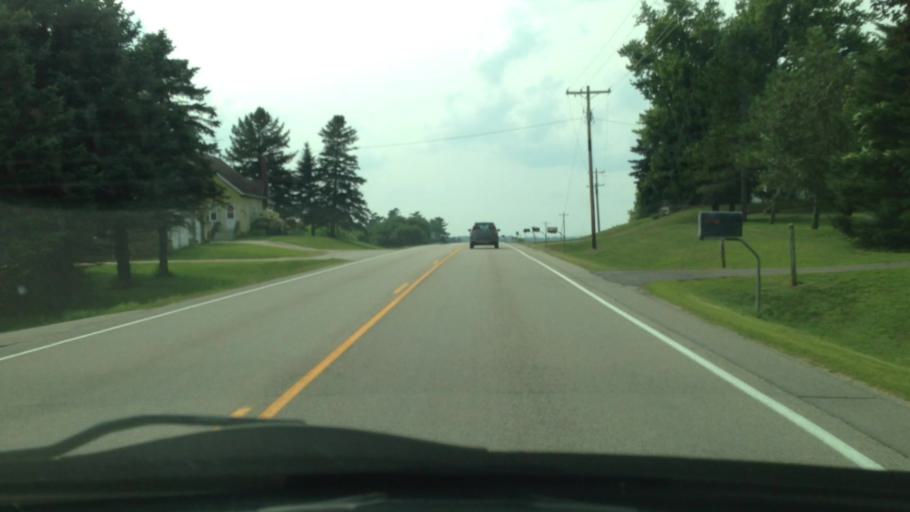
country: US
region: Minnesota
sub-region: Wabasha County
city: Elgin
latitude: 44.1657
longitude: -92.3401
